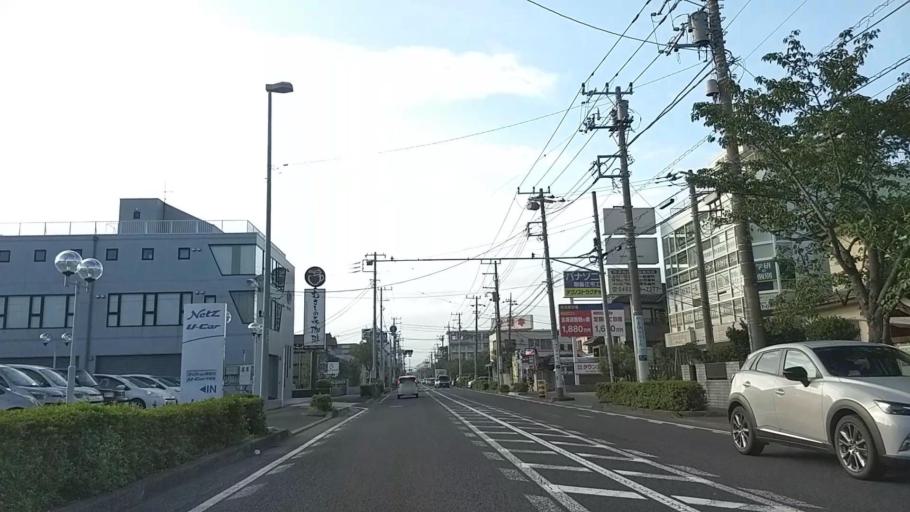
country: JP
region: Kanagawa
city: Hiratsuka
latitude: 35.3290
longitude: 139.3284
